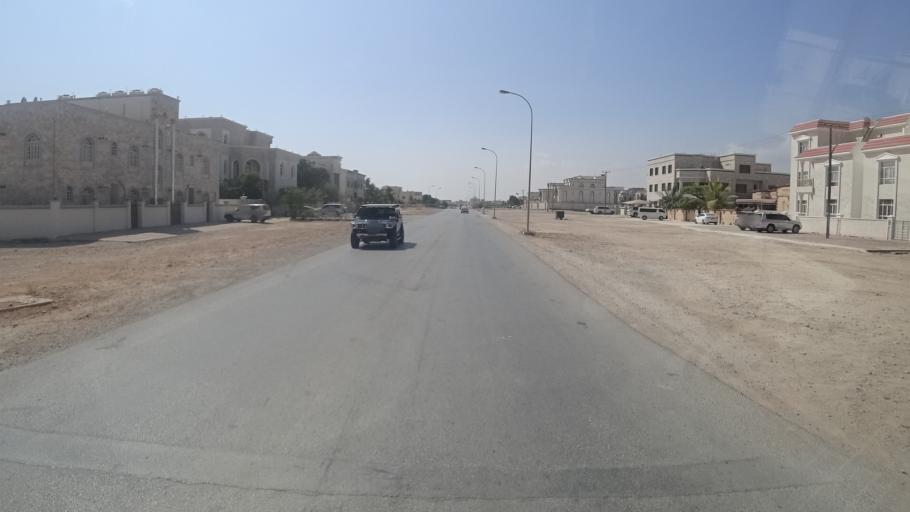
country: OM
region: Zufar
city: Salalah
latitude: 17.0182
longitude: 54.0298
